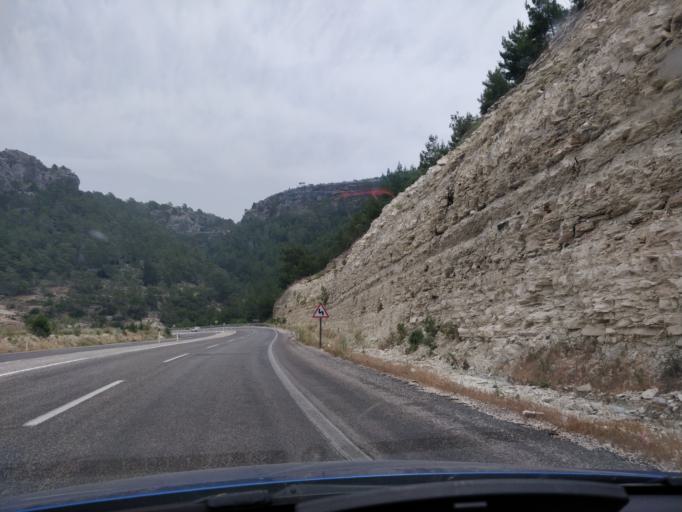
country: TR
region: Mersin
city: Tasucu
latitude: 36.3973
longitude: 33.8536
